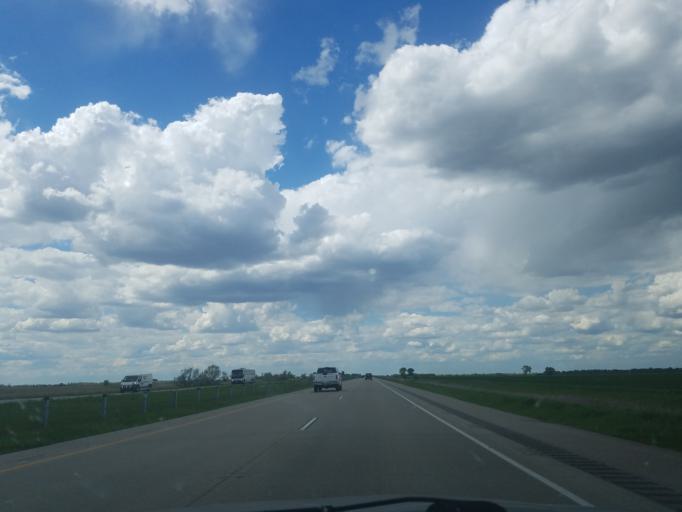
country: US
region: Minnesota
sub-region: Clay County
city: Barnesville
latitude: 46.6984
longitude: -96.4569
